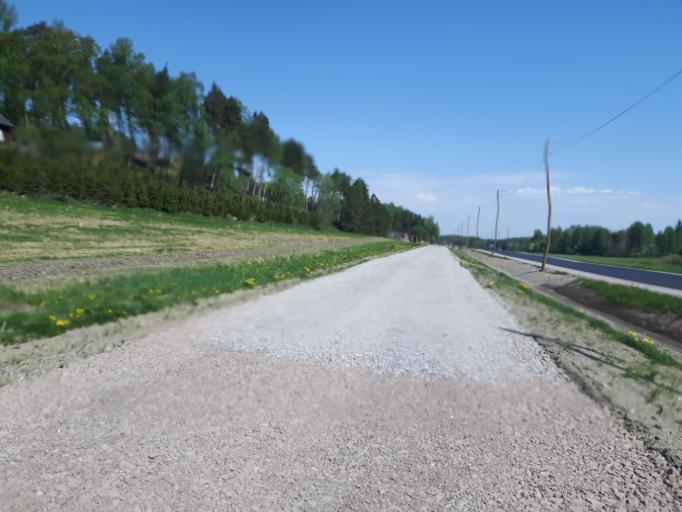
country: FI
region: Uusimaa
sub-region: Helsinki
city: Pornainen
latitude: 60.3458
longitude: 25.4883
